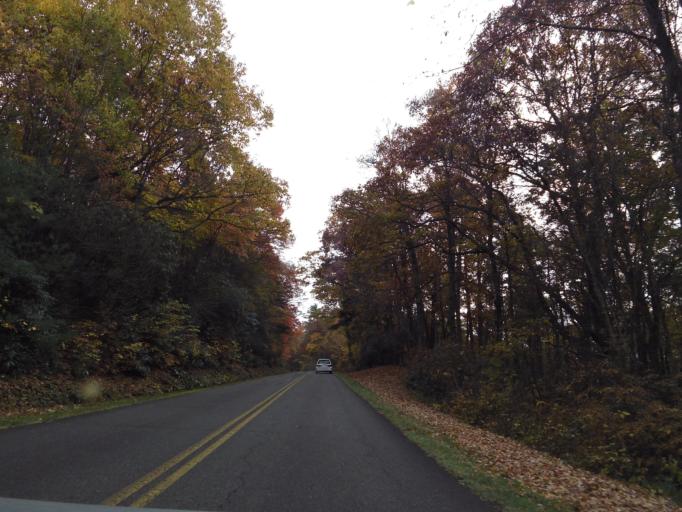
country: US
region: North Carolina
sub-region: Ashe County
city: Jefferson
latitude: 36.3080
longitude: -81.3617
